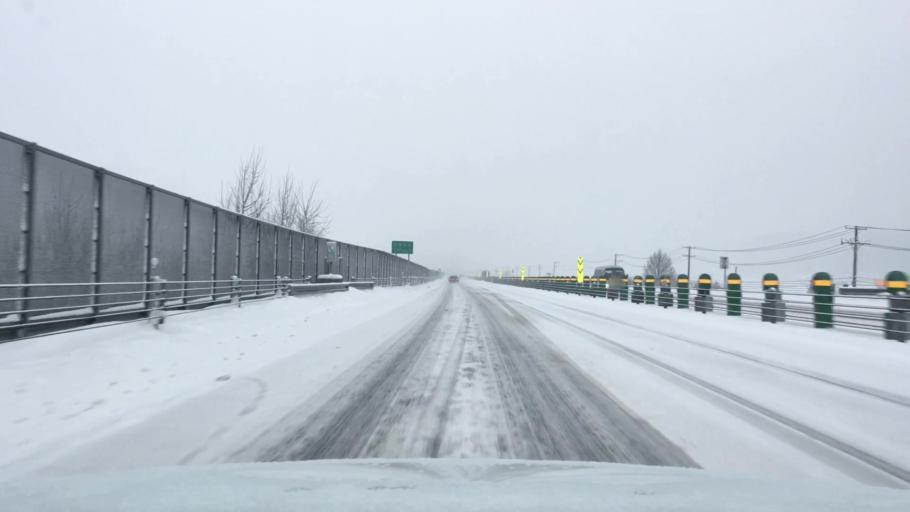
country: JP
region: Akita
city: Hanawa
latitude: 40.2805
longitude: 140.7609
